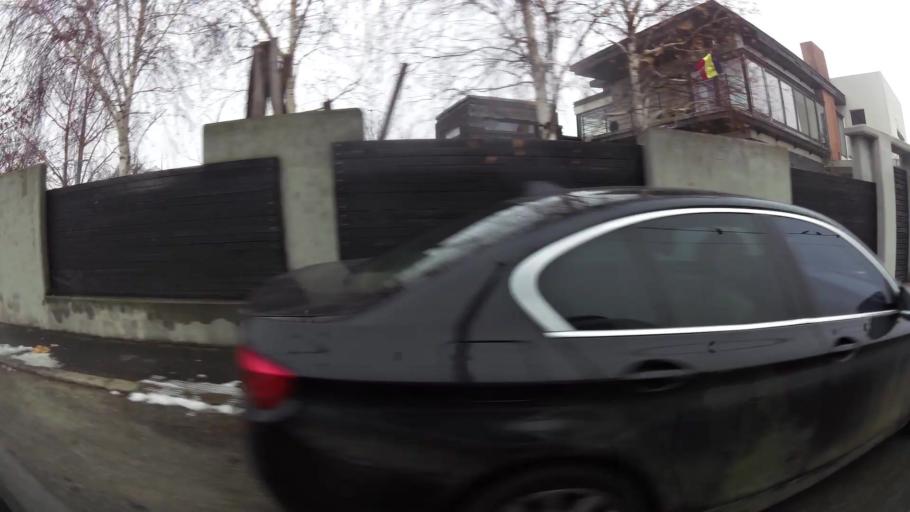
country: RO
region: Ilfov
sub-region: Comuna Chiajna
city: Rosu
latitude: 44.4533
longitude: 26.0133
